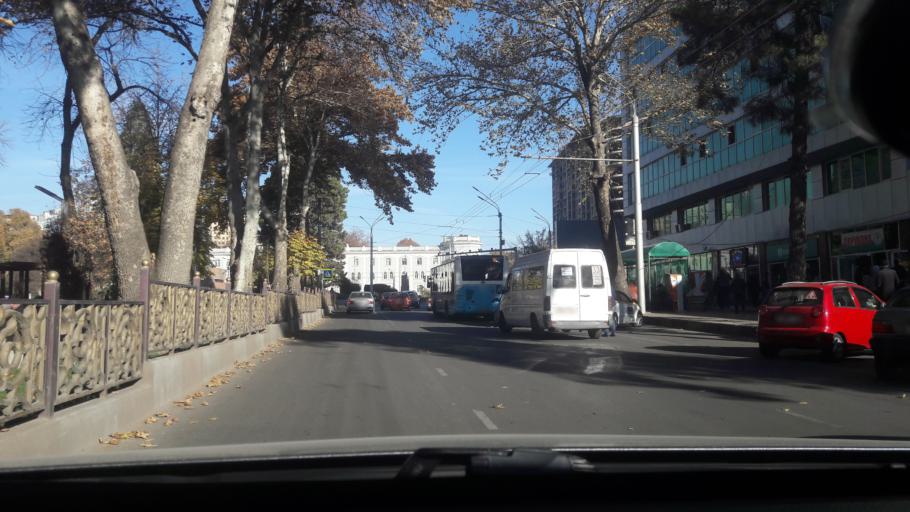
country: TJ
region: Dushanbe
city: Dushanbe
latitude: 38.5613
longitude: 68.7995
